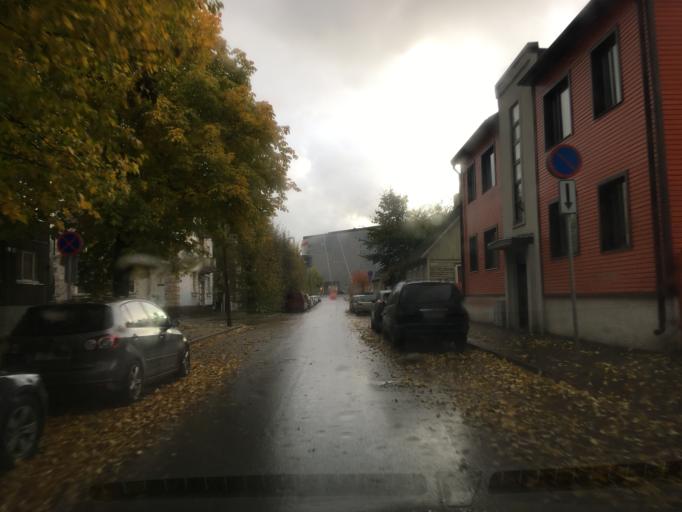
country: EE
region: Harju
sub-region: Tallinna linn
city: Tallinn
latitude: 59.4264
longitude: 24.7911
